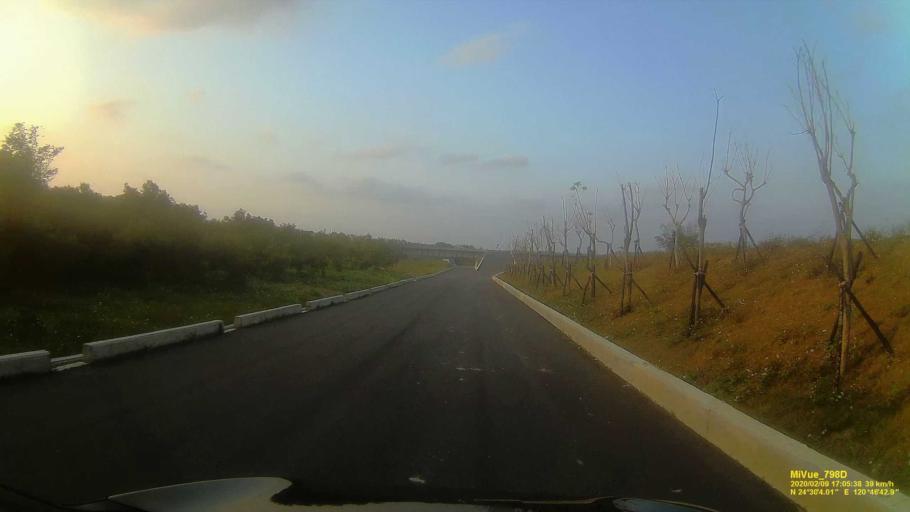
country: TW
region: Taiwan
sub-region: Miaoli
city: Miaoli
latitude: 24.5013
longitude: 120.7785
